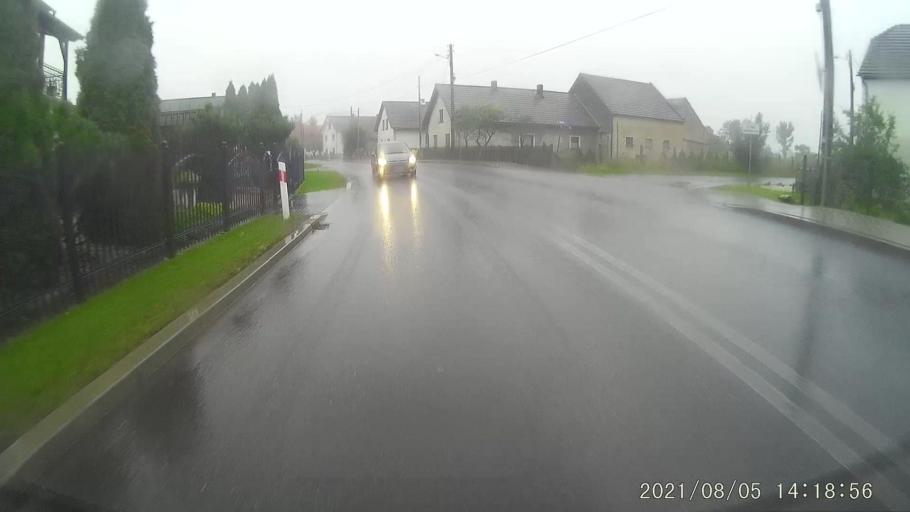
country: PL
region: Opole Voivodeship
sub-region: Powiat prudnicki
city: Biala
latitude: 50.4650
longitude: 17.6901
